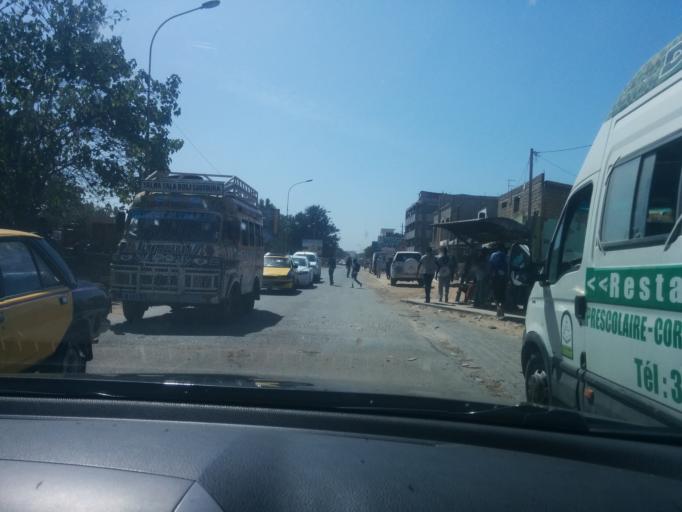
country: SN
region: Dakar
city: Grand Dakar
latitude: 14.7363
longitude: -17.4455
